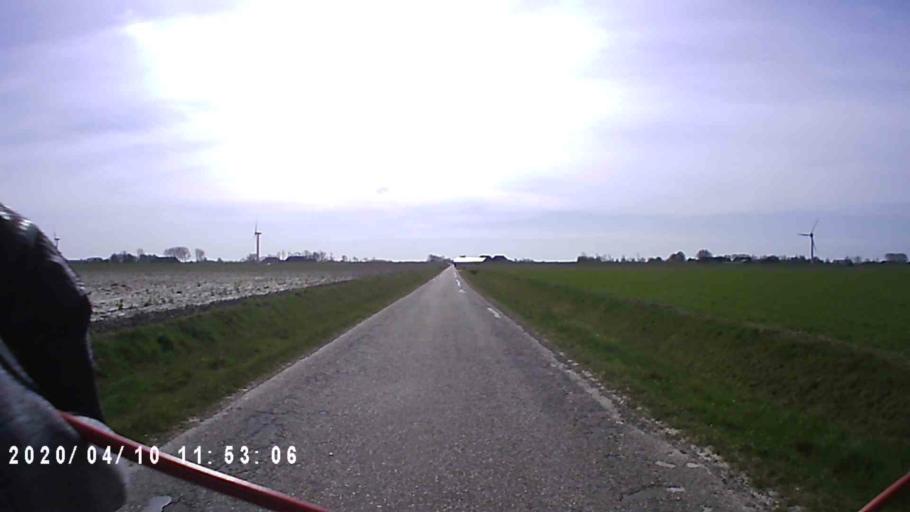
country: NL
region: Groningen
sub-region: Gemeente De Marne
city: Ulrum
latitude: 53.3920
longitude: 6.3325
